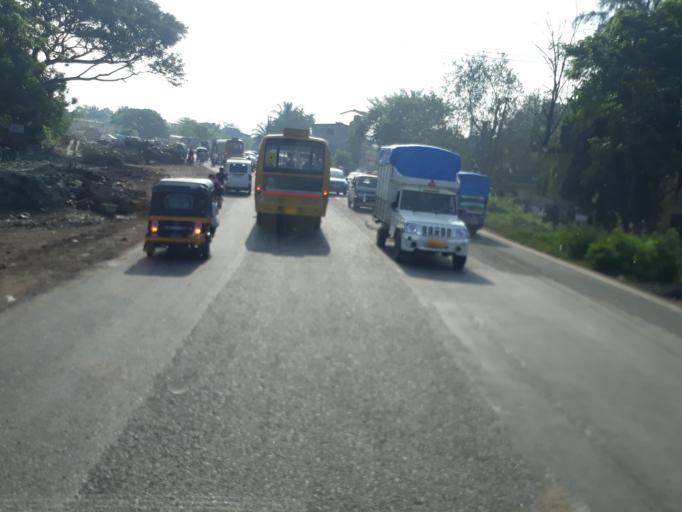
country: IN
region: Maharashtra
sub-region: Raigarh
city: Kalundri
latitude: 18.9752
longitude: 73.1183
